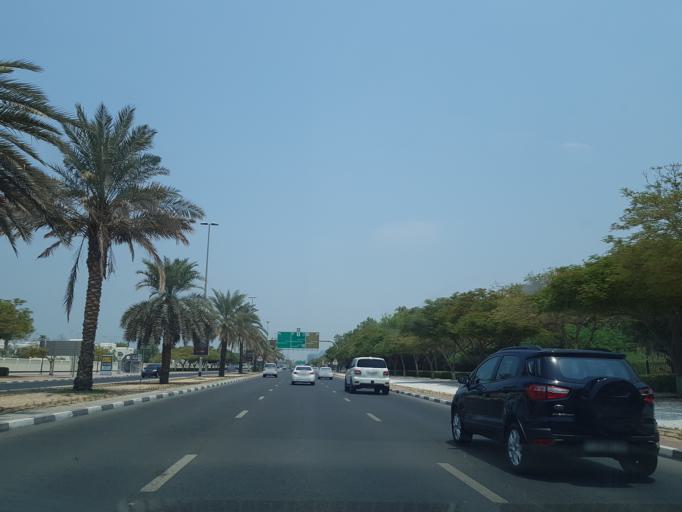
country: AE
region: Ash Shariqah
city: Sharjah
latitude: 25.2377
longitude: 55.3246
